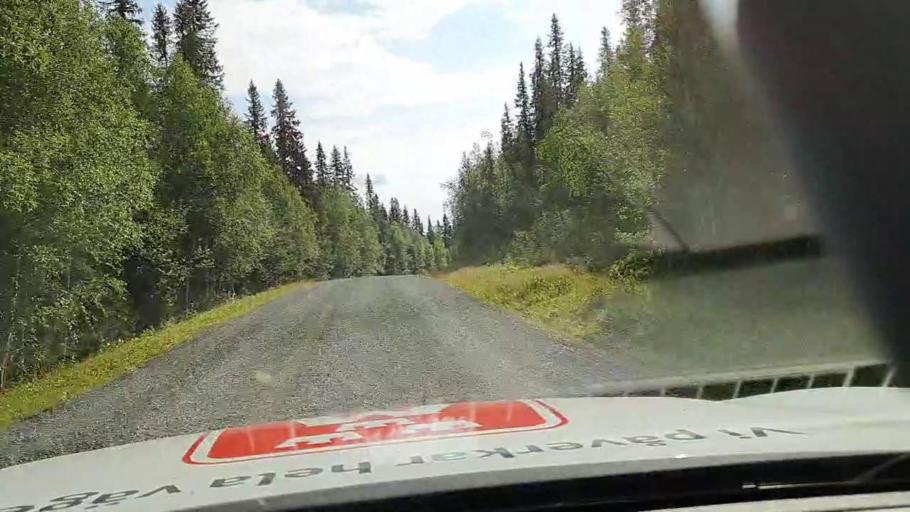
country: SE
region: Vaesterbotten
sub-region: Storumans Kommun
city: Fristad
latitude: 65.5379
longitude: 16.8080
